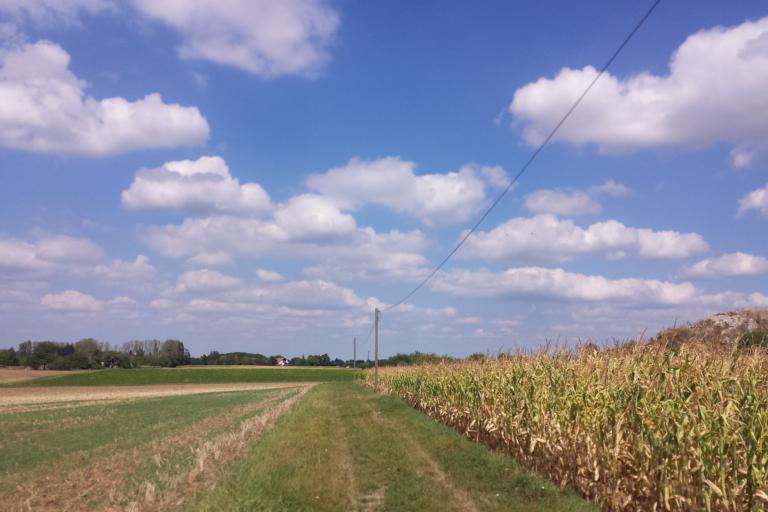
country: DE
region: Hesse
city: Viernheim
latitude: 49.5196
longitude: 8.5832
